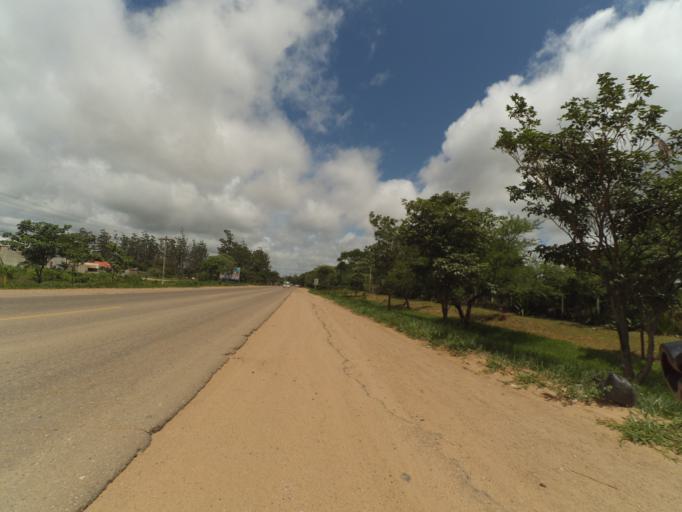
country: BO
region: Santa Cruz
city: Santa Rita
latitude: -17.8727
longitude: -63.2718
